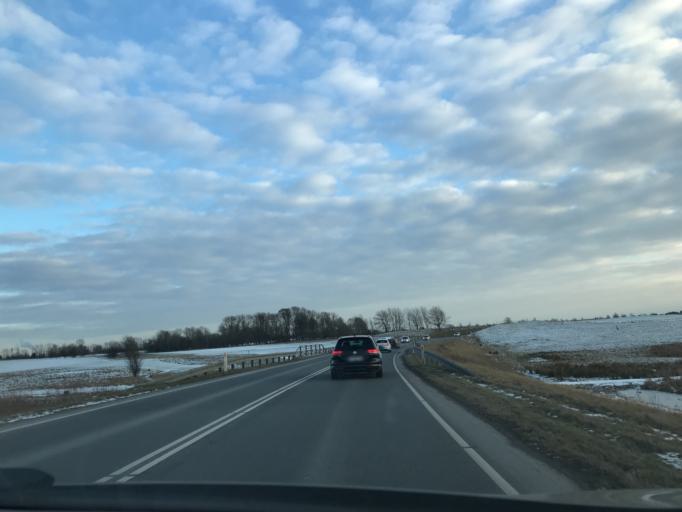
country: DK
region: Capital Region
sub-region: Egedal Kommune
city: Smorumnedre
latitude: 55.7272
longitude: 12.3124
